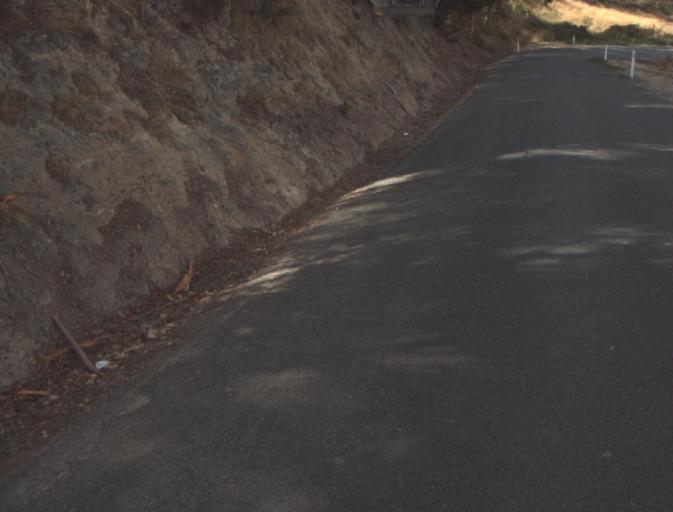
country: AU
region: Tasmania
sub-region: Launceston
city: Mayfield
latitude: -41.2452
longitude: 147.1512
